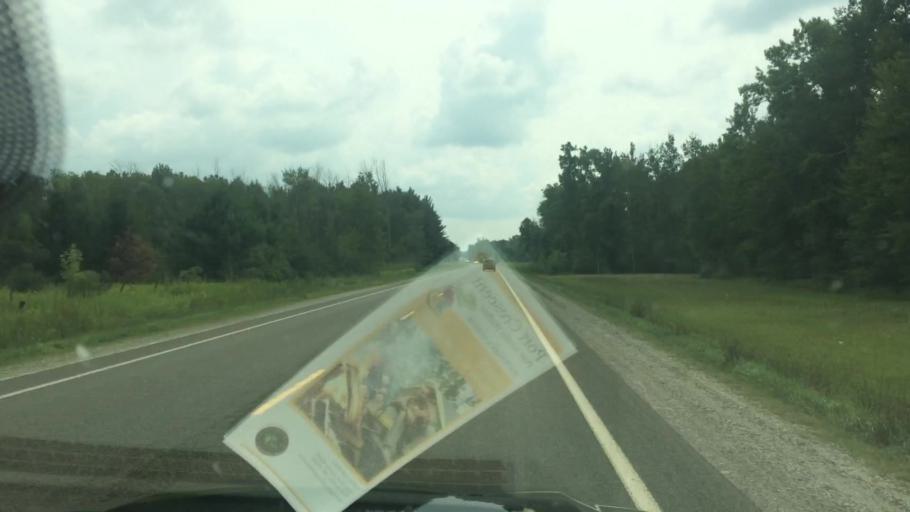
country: US
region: Michigan
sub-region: Tuscola County
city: Cass City
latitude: 43.6516
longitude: -83.0983
